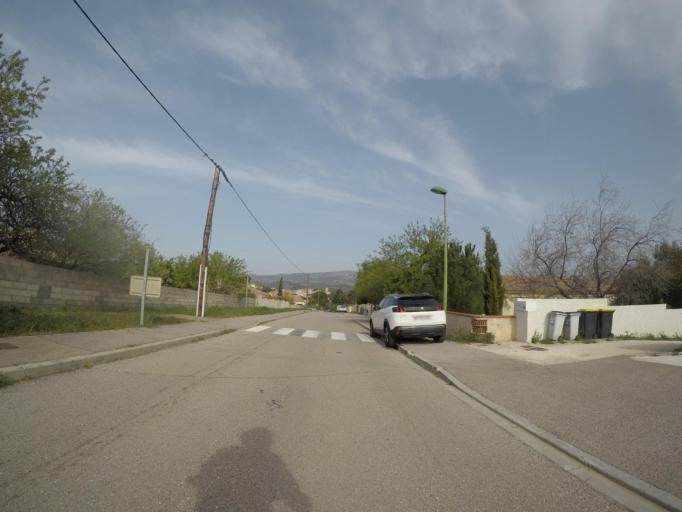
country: FR
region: Languedoc-Roussillon
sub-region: Departement des Pyrenees-Orientales
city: Baixas
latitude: 42.7751
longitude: 2.7940
